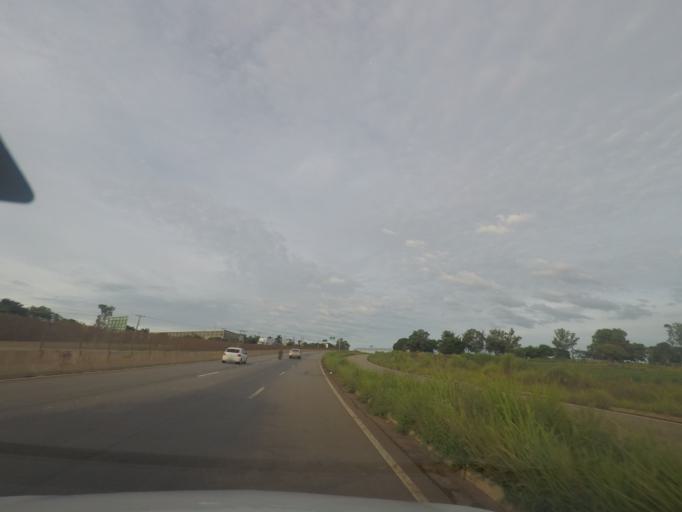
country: BR
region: Goias
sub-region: Trindade
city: Trindade
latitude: -16.7287
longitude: -49.3846
